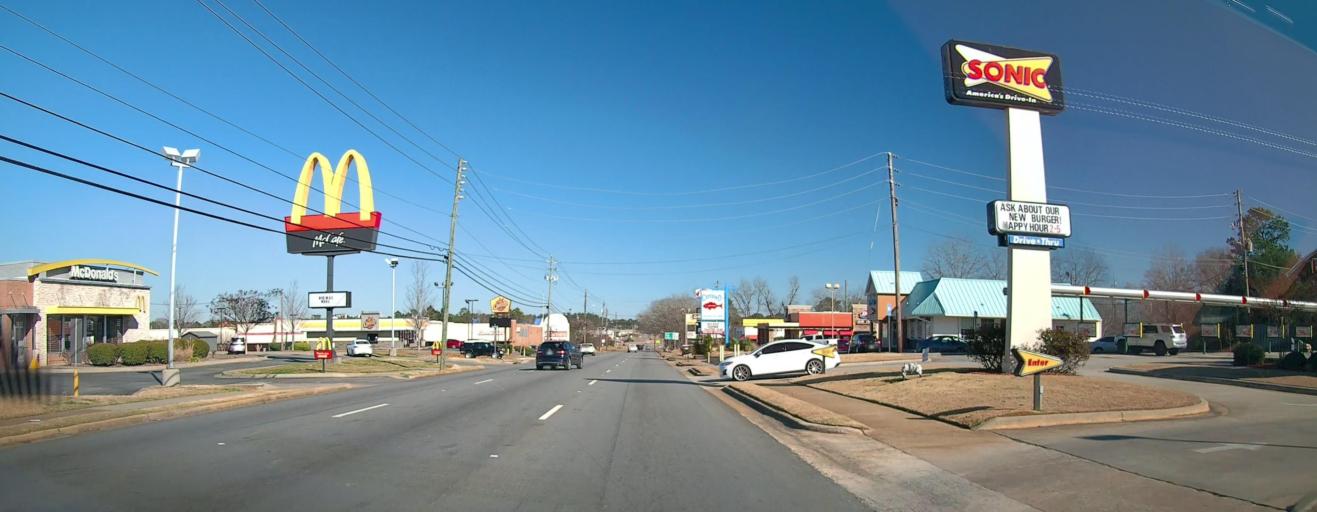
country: US
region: Georgia
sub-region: Sumter County
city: Americus
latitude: 32.0712
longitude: -84.2168
